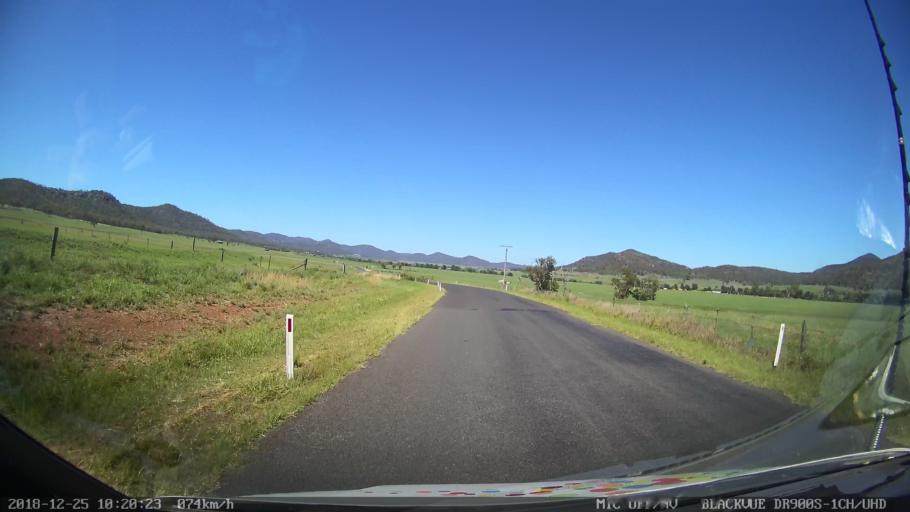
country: AU
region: New South Wales
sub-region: Muswellbrook
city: Denman
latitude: -32.3577
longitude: 150.5494
